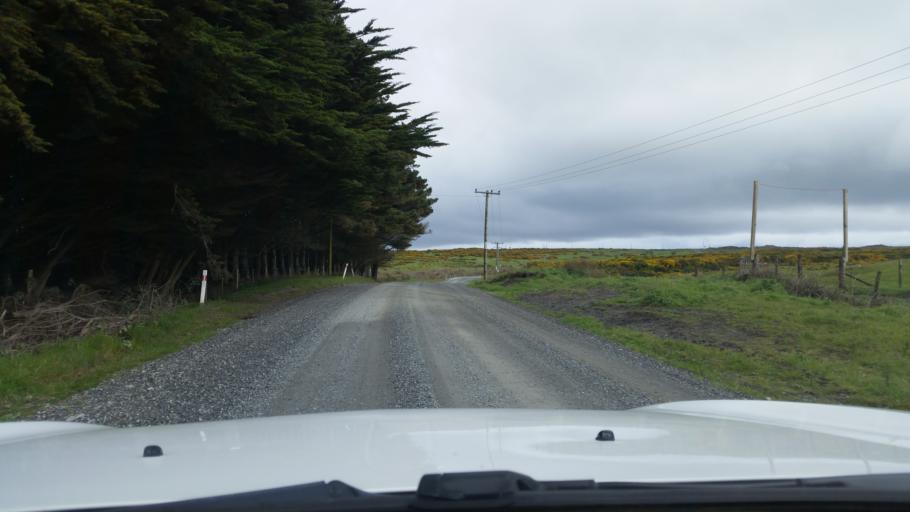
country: NZ
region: Chatham Islands
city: Waitangi
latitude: -43.8472
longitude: -176.5256
